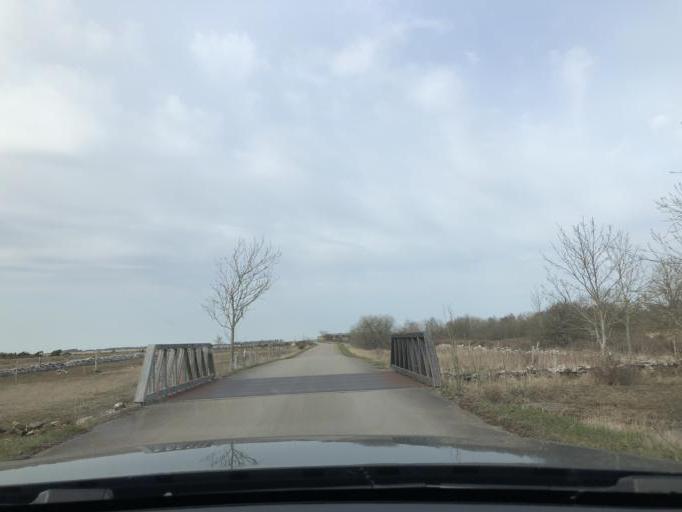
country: SE
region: Kalmar
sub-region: Morbylanga Kommun
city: Moerbylanga
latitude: 56.2901
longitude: 16.4821
